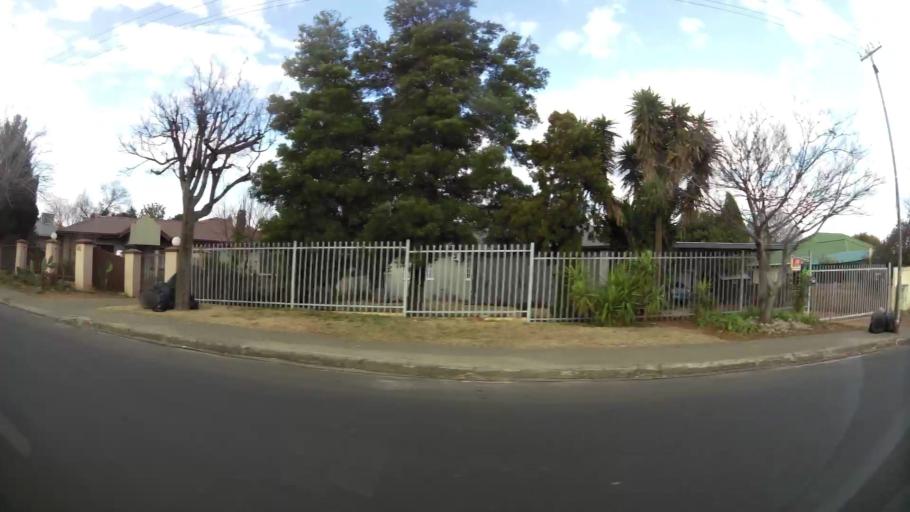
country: ZA
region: Orange Free State
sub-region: Mangaung Metropolitan Municipality
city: Bloemfontein
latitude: -29.0899
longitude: 26.2042
